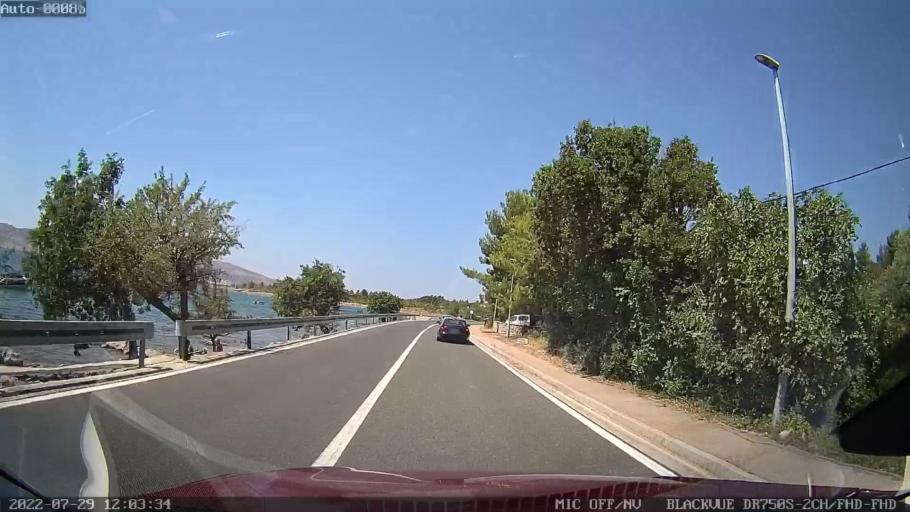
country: HR
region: Zadarska
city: Posedarje
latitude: 44.2737
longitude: 15.5087
